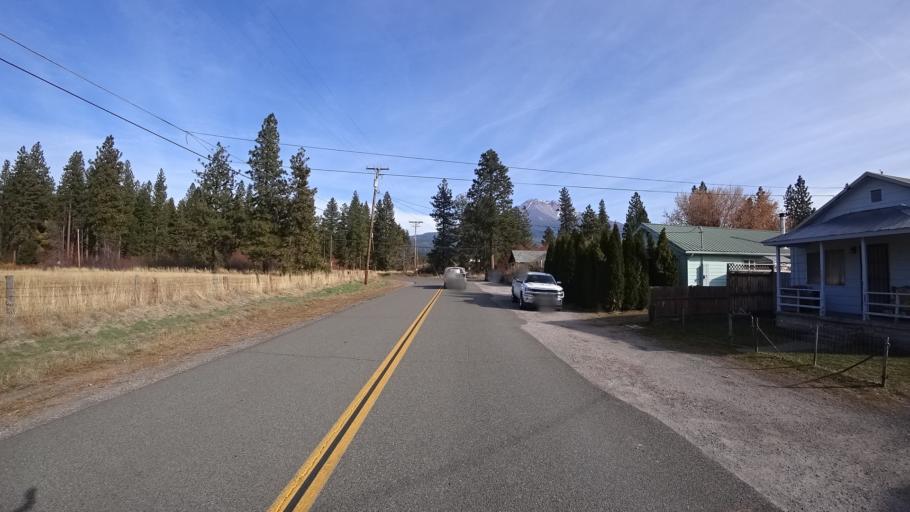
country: US
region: California
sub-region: Siskiyou County
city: Weed
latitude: 41.4392
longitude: -122.3774
